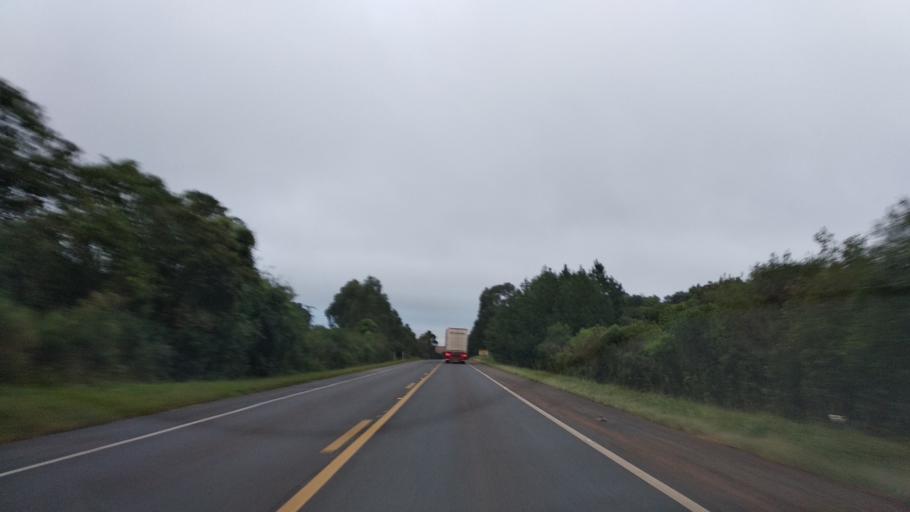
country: BR
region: Santa Catarina
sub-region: Campos Novos
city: Campos Novos
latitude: -27.3800
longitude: -51.0974
